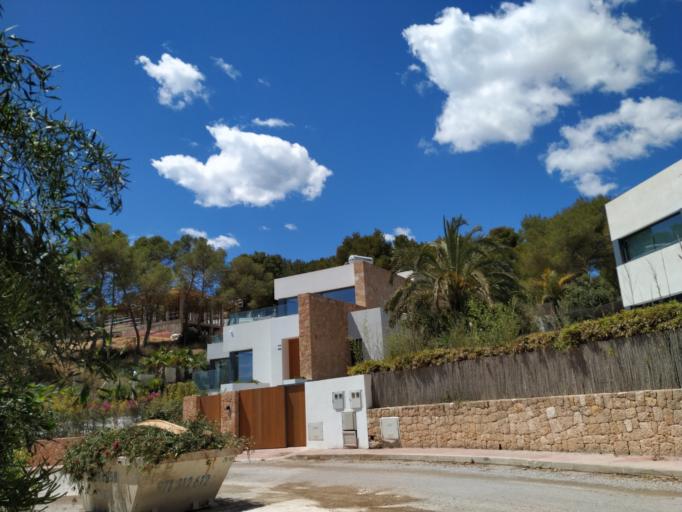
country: ES
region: Balearic Islands
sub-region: Illes Balears
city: Ibiza
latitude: 38.9195
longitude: 1.4727
